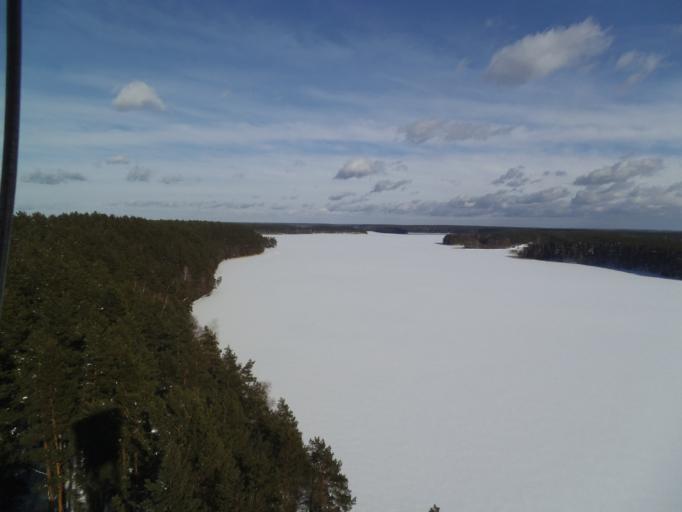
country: LT
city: Moletai
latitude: 55.2146
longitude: 25.5360
